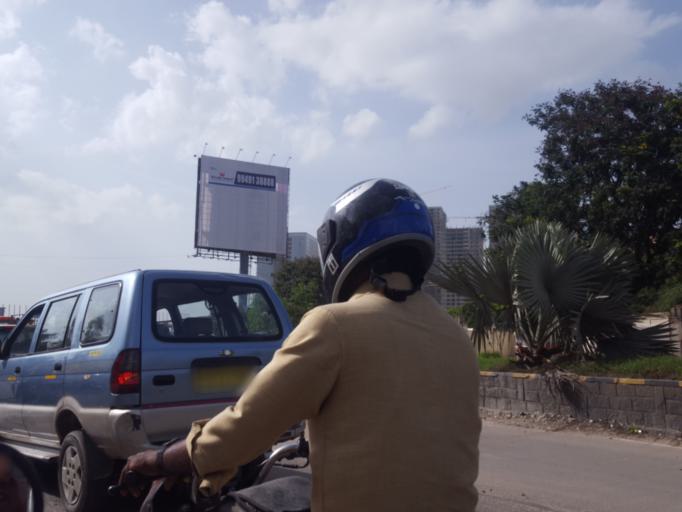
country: IN
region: Telangana
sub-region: Rangareddi
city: Kukatpalli
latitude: 17.4254
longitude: 78.3785
